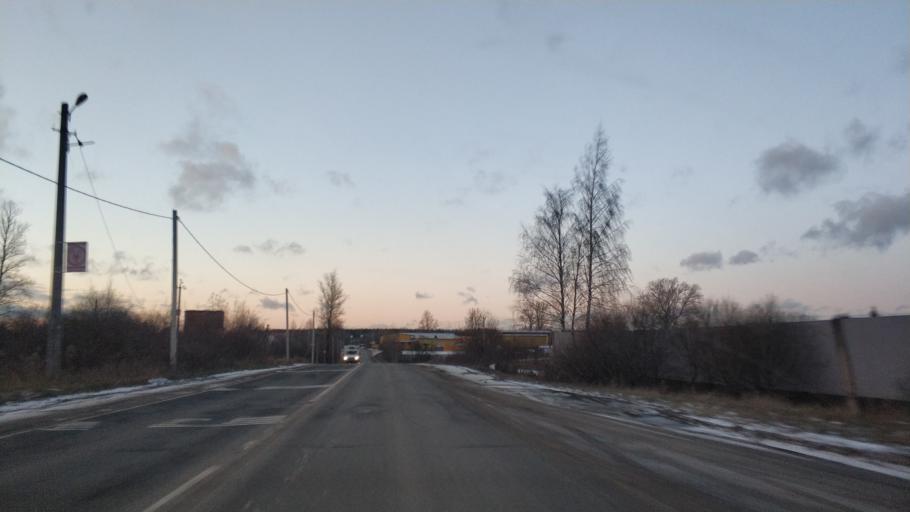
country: RU
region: St.-Petersburg
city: Pontonnyy
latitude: 59.8123
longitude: 30.6083
